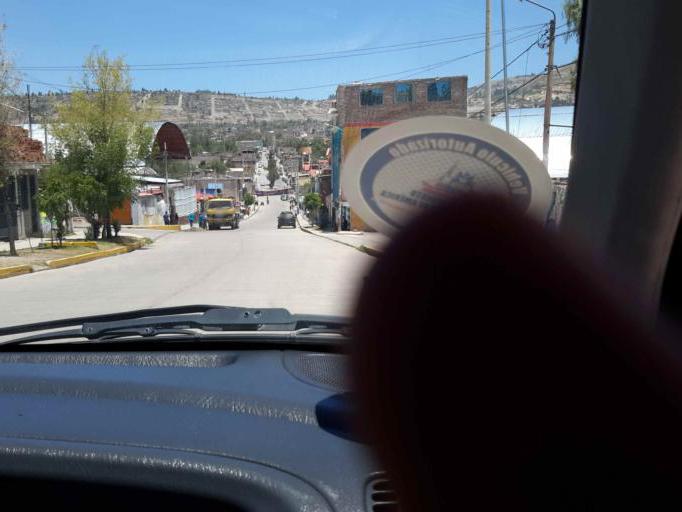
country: PE
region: Ayacucho
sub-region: Provincia de Huamanga
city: Carmen Alto
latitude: -13.1737
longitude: -74.2216
